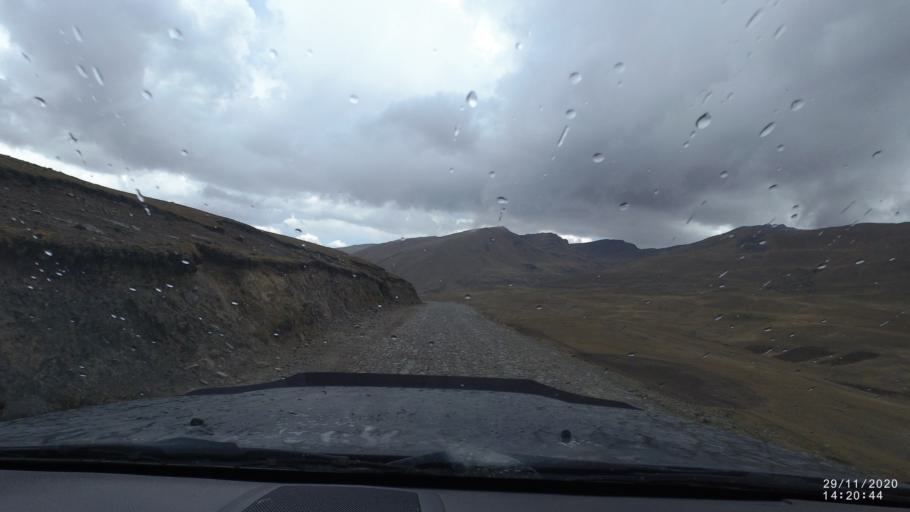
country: BO
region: Cochabamba
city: Sipe Sipe
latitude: -17.2500
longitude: -66.3915
